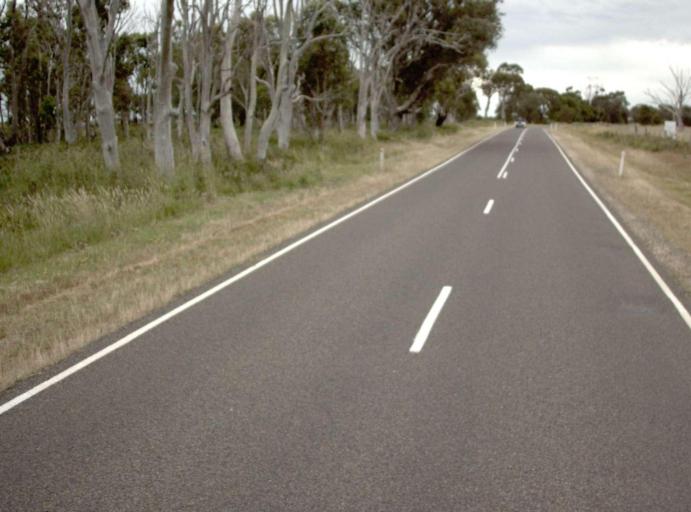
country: AU
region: Victoria
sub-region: East Gippsland
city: Bairnsdale
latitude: -37.9685
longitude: 147.4791
